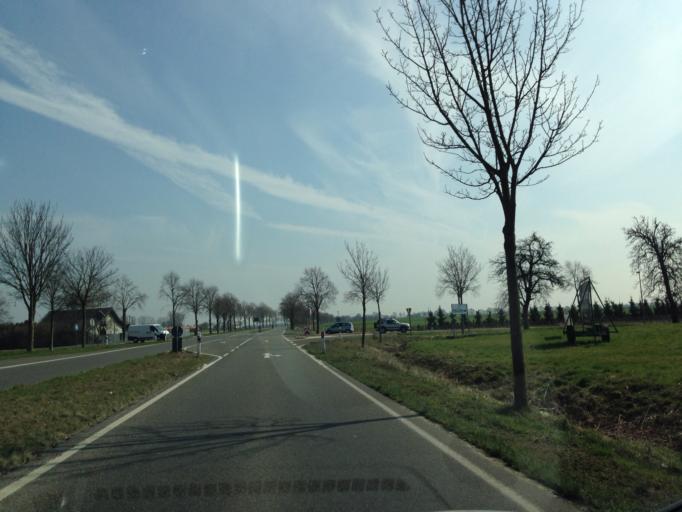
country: DE
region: North Rhine-Westphalia
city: Huckelhoven
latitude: 51.0922
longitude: 6.2615
